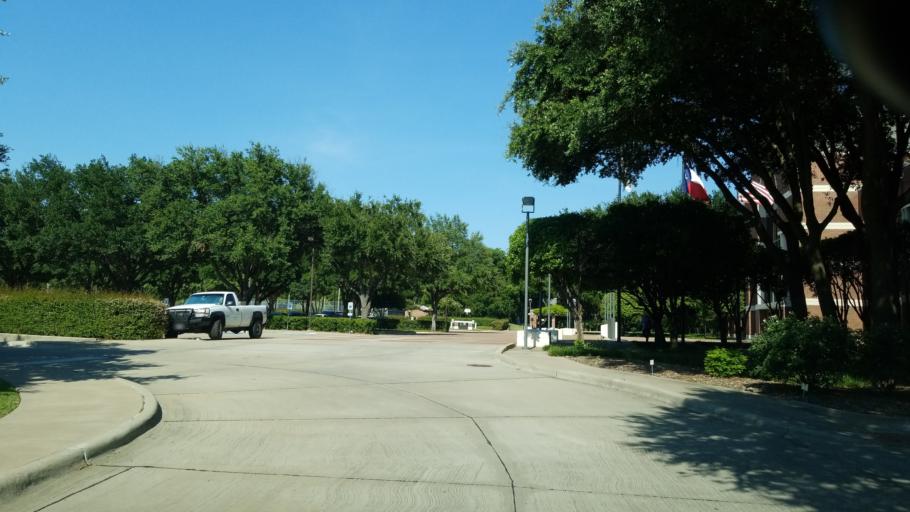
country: US
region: Texas
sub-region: Dallas County
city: Farmers Branch
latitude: 32.9213
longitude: -96.8939
